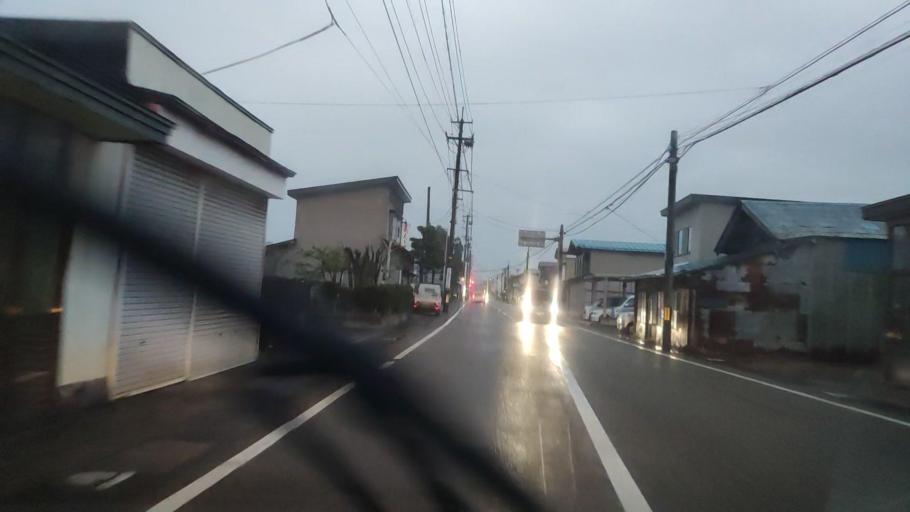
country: JP
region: Akita
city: Omagari
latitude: 39.4710
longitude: 140.4709
